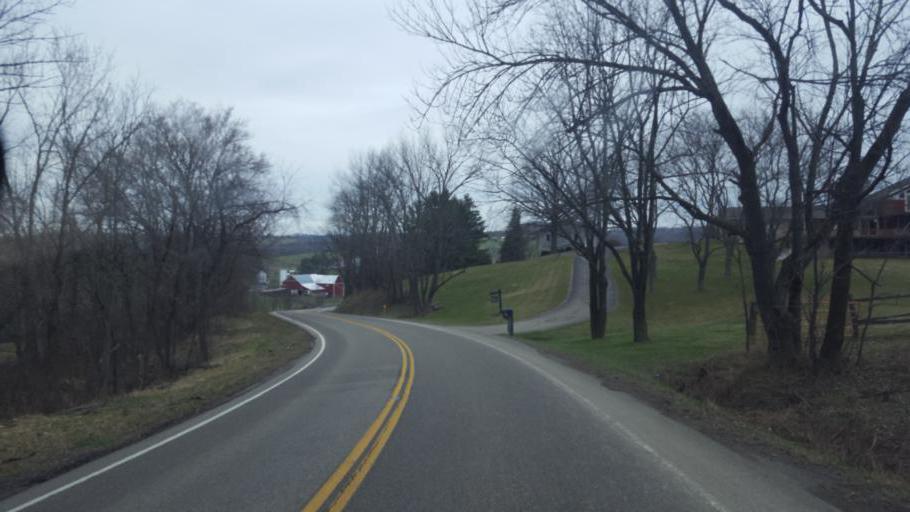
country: US
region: Ohio
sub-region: Tuscarawas County
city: Sugarcreek
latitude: 40.5440
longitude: -81.7197
